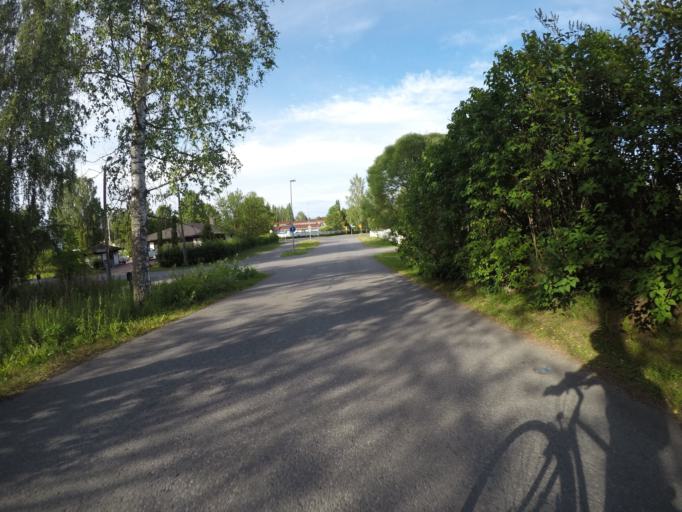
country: FI
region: Haeme
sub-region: Haemeenlinna
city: Haemeenlinna
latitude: 60.9806
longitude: 24.4194
